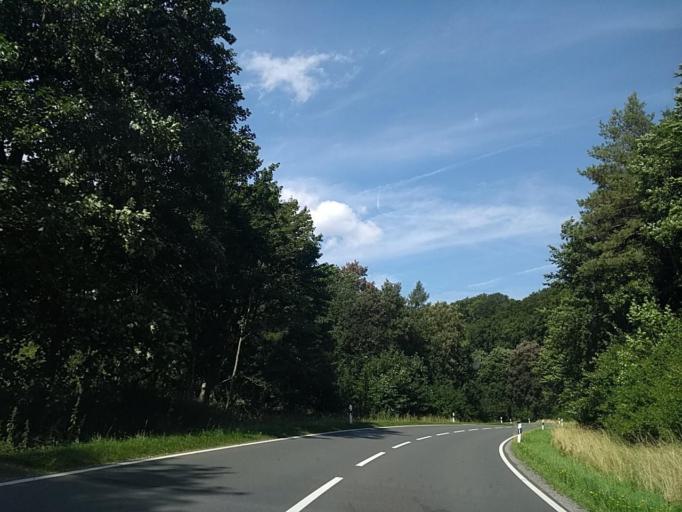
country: DE
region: North Rhine-Westphalia
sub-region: Regierungsbezirk Arnsberg
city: Brilon
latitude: 51.4443
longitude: 8.6378
